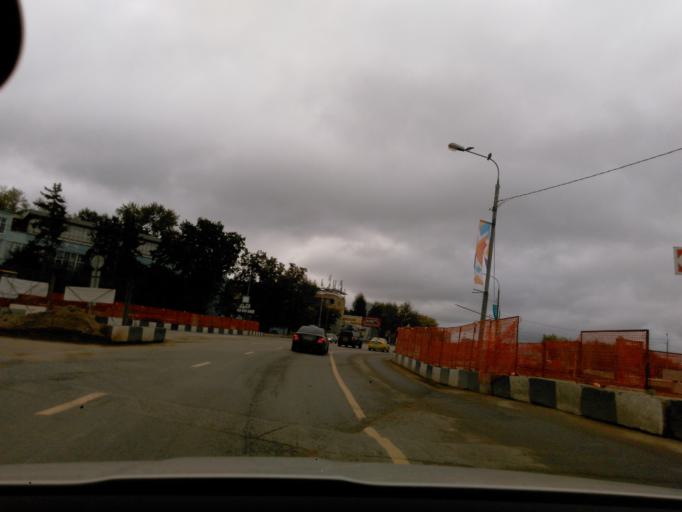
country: RU
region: Moscow
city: Pokrovskoye-Streshnevo
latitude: 55.8229
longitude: 37.4397
